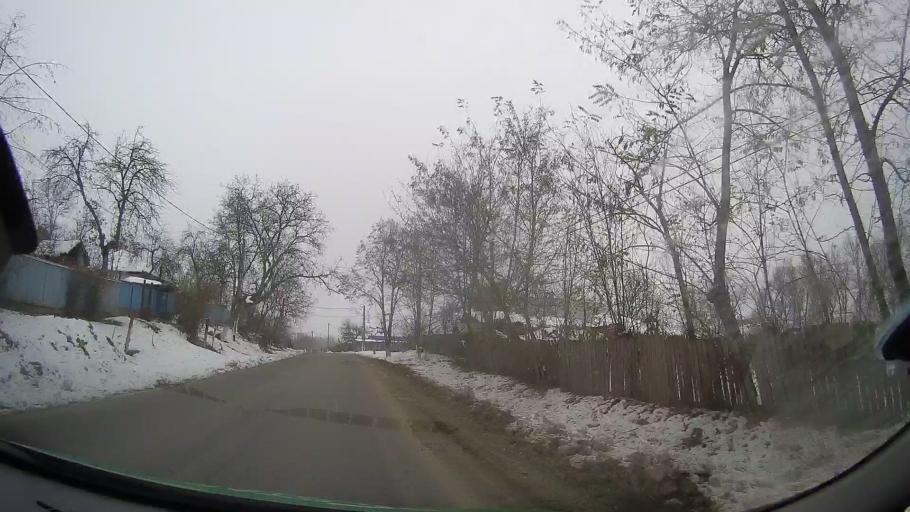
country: RO
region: Bacau
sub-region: Comuna Glavanesti
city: Frumuselu
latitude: 46.2887
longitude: 27.3007
